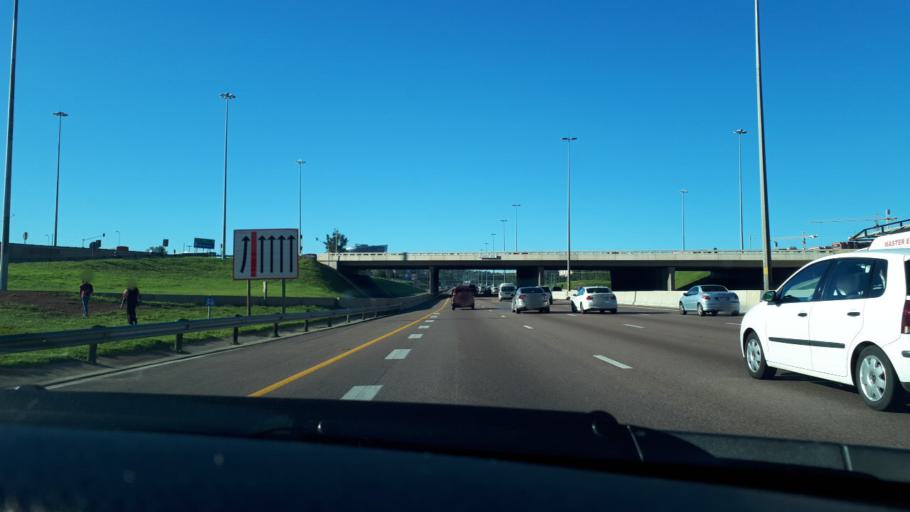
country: ZA
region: Gauteng
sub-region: City of Tshwane Metropolitan Municipality
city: Pretoria
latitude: -25.7771
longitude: 28.2723
